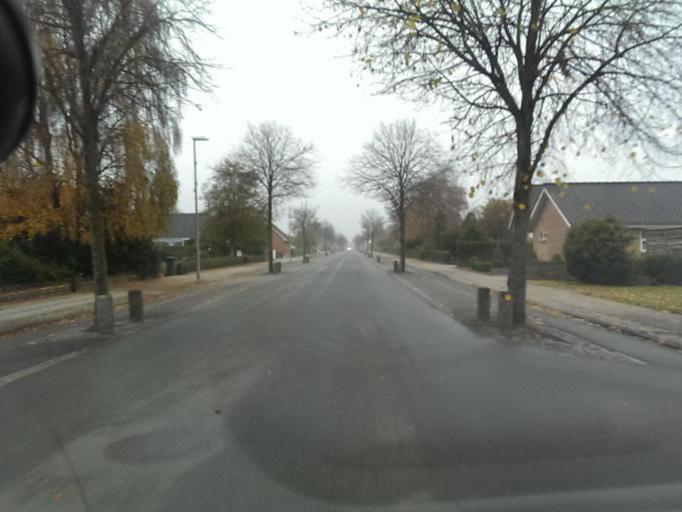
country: DK
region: South Denmark
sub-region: Esbjerg Kommune
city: Bramming
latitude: 55.4660
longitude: 8.6943
